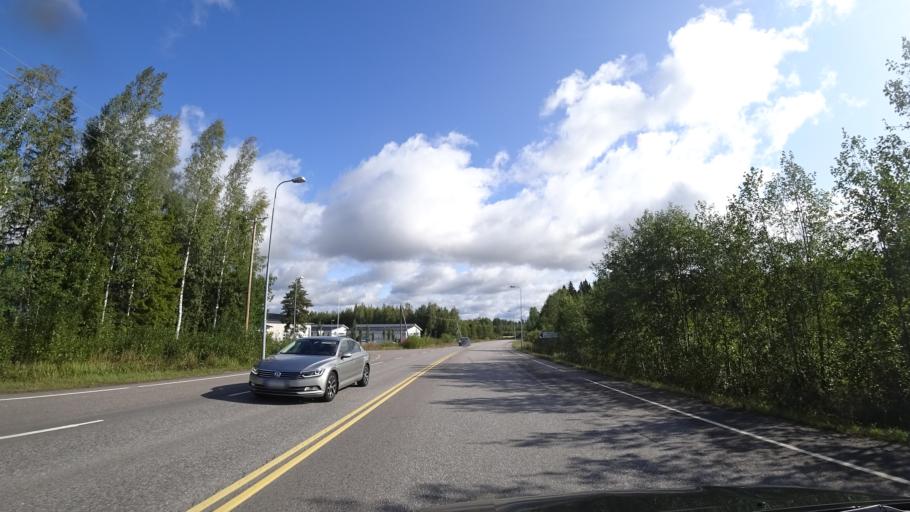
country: FI
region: Uusimaa
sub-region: Helsinki
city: Hyvinge
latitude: 60.5490
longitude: 24.9425
